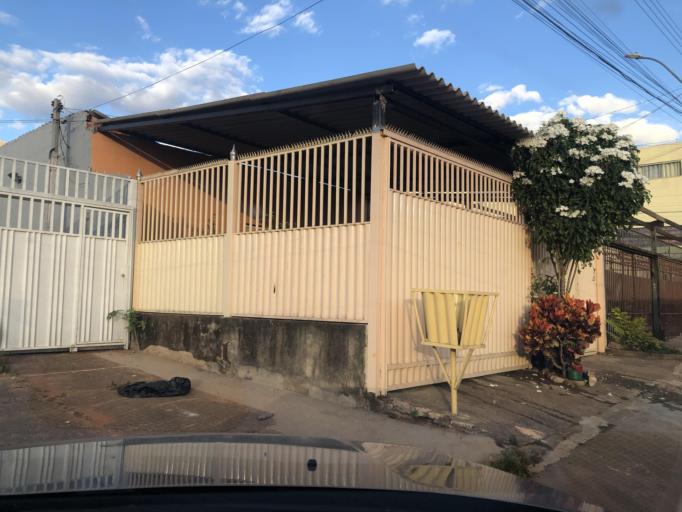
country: BR
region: Federal District
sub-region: Brasilia
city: Brasilia
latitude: -15.8715
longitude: -48.0958
